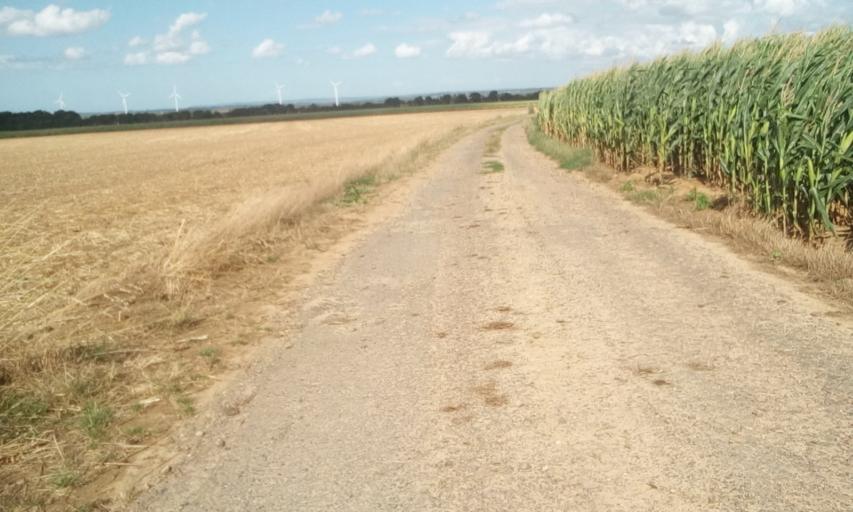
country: FR
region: Lower Normandy
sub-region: Departement du Calvados
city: Saint-Sylvain
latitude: 49.0721
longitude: -0.2472
